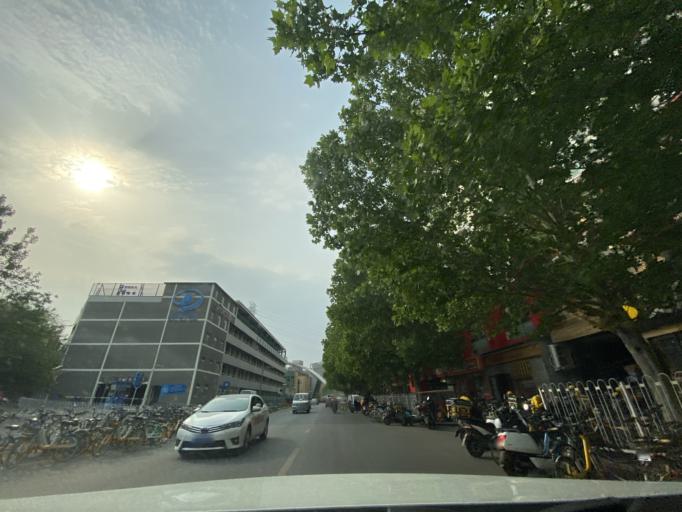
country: CN
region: Beijing
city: Haidian
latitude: 39.9756
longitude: 116.3368
